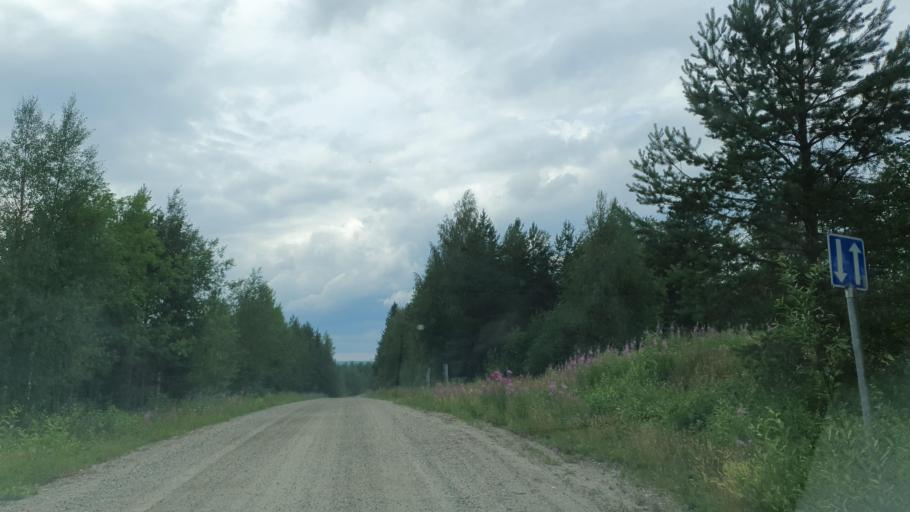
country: FI
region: Kainuu
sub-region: Kehys-Kainuu
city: Kuhmo
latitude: 64.4876
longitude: 29.7148
